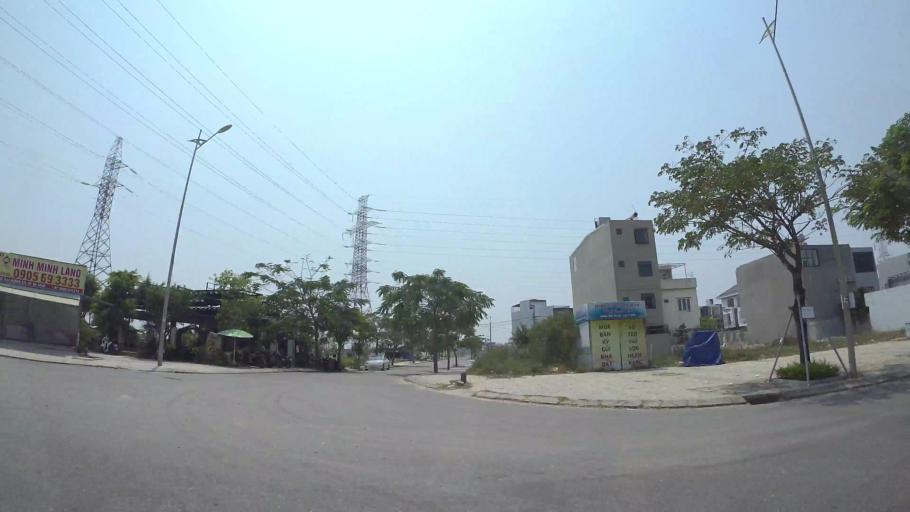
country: VN
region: Da Nang
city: Ngu Hanh Son
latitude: 16.0161
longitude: 108.2338
